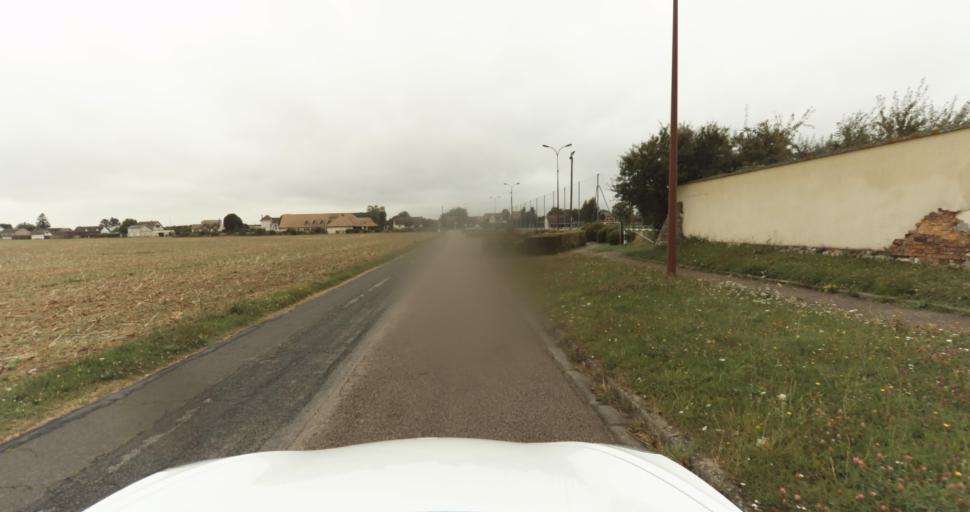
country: FR
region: Haute-Normandie
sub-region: Departement de l'Eure
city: Aviron
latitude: 49.0572
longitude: 1.1218
